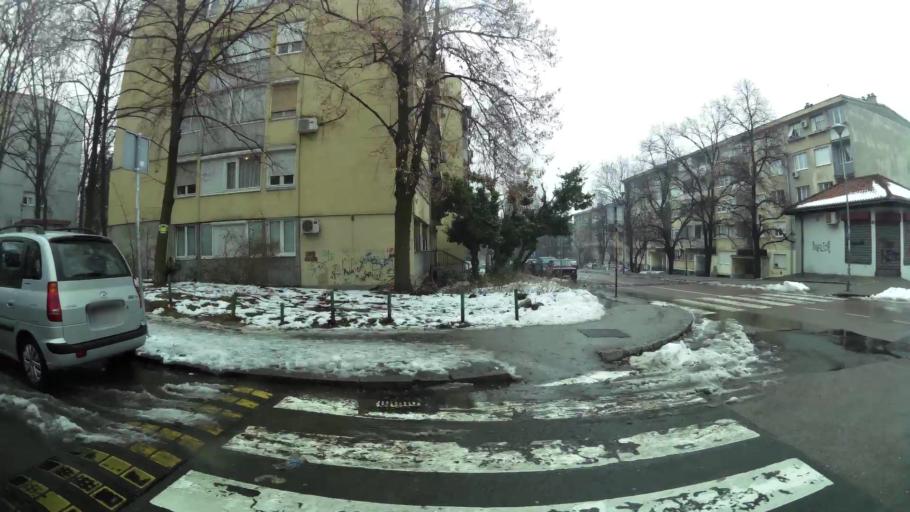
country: RS
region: Central Serbia
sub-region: Belgrade
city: Vozdovac
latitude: 44.7693
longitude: 20.4920
